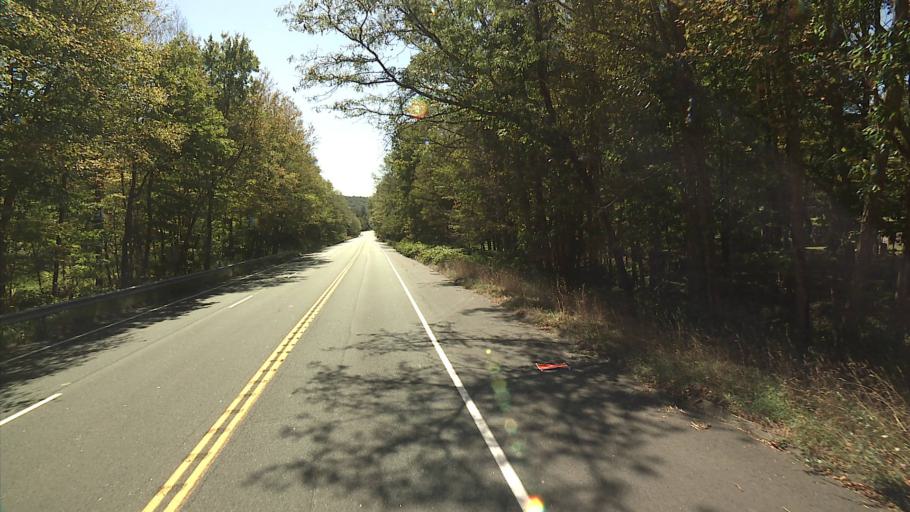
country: US
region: Connecticut
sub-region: New Haven County
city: Woodbridge
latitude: 41.3960
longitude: -72.9739
